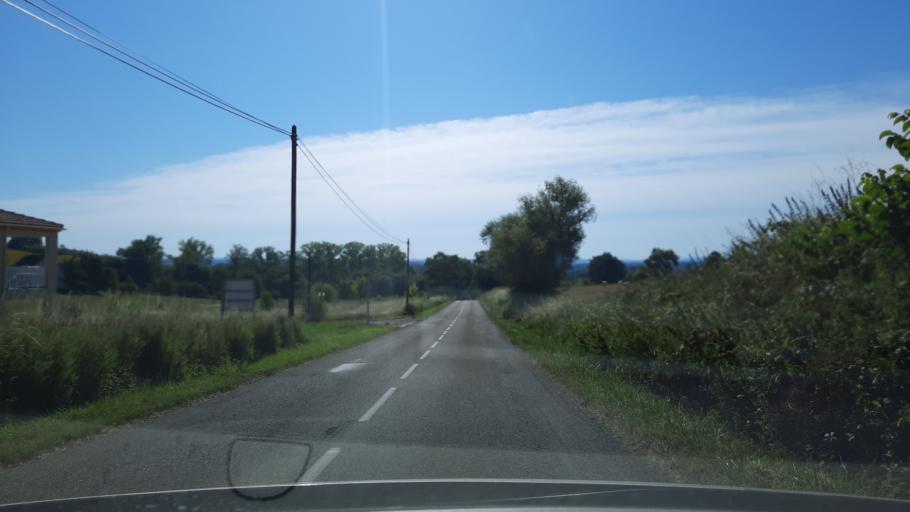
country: FR
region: Midi-Pyrenees
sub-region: Departement du Tarn-et-Garonne
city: Caussade
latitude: 44.1695
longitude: 1.5191
